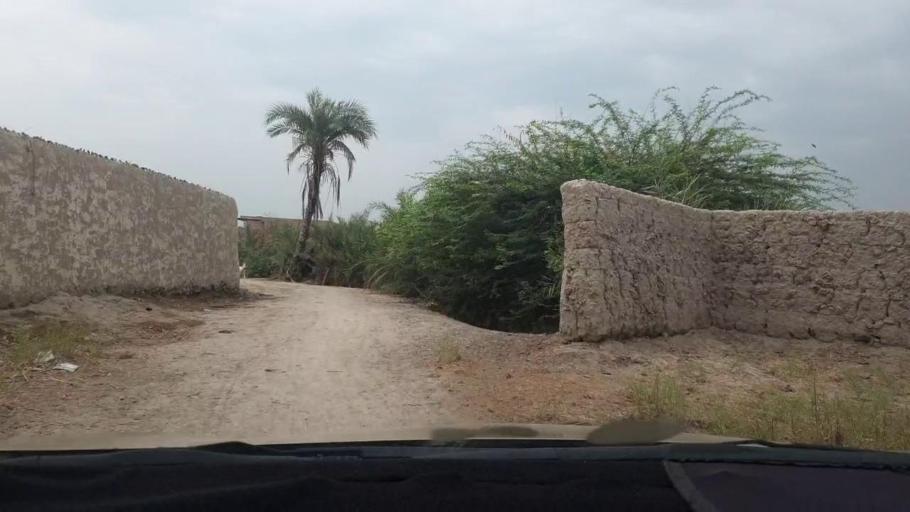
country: PK
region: Sindh
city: Larkana
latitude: 27.5779
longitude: 68.2424
